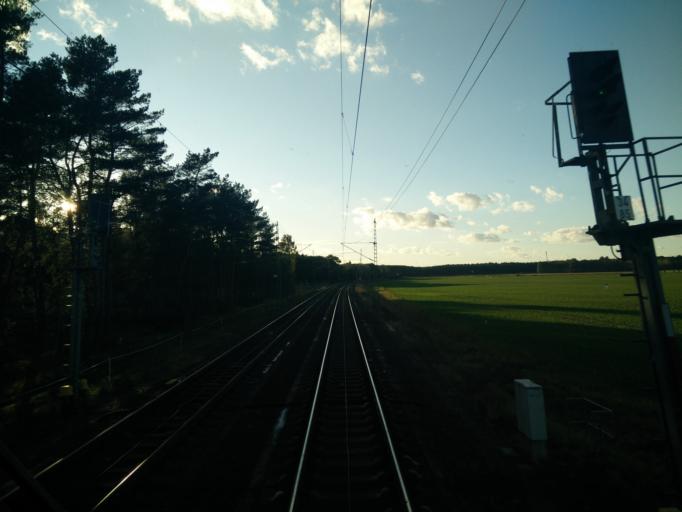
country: DE
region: Brandenburg
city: Breddin
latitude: 52.8907
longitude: 12.1491
